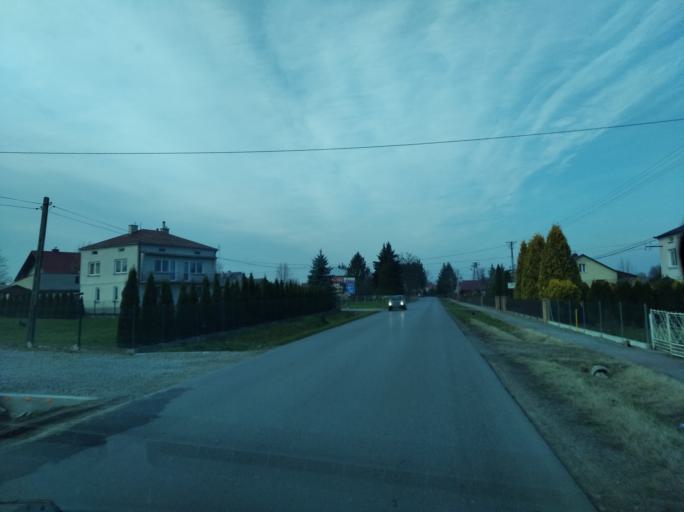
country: PL
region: Subcarpathian Voivodeship
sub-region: Powiat ropczycko-sedziszowski
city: Iwierzyce
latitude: 50.0526
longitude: 21.7453
